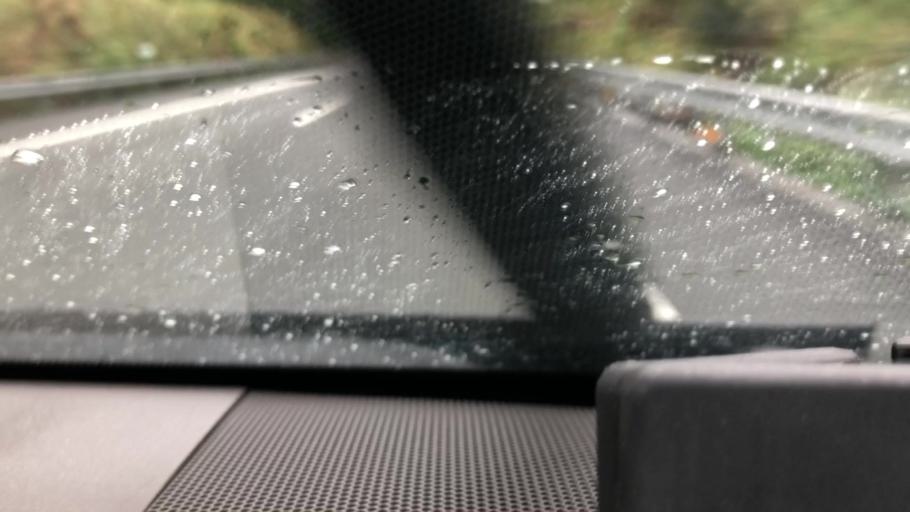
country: JP
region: Shizuoka
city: Mishima
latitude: 35.1898
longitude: 138.8889
